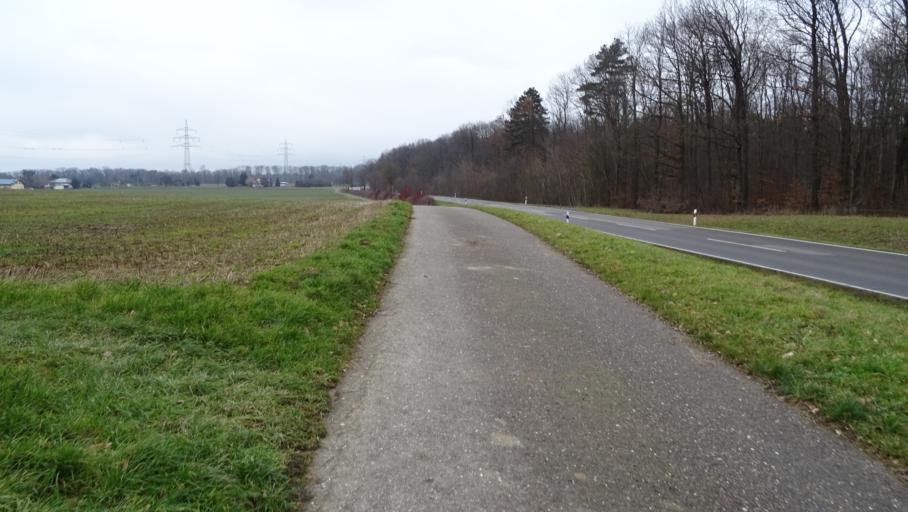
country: DE
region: Baden-Wuerttemberg
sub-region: Karlsruhe Region
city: Huffenhardt
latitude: 49.3164
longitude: 9.0745
